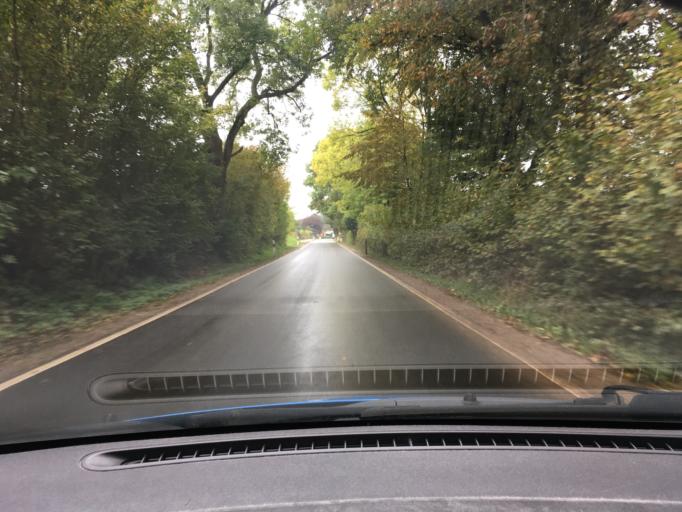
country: DE
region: Schleswig-Holstein
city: Nehmten
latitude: 54.0775
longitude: 10.3902
